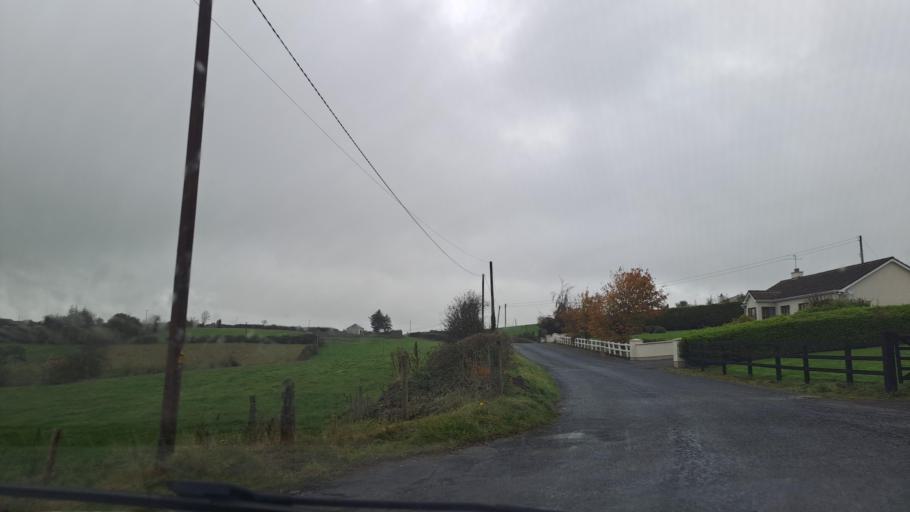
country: IE
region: Ulster
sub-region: An Cabhan
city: Kingscourt
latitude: 53.9569
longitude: -6.8809
